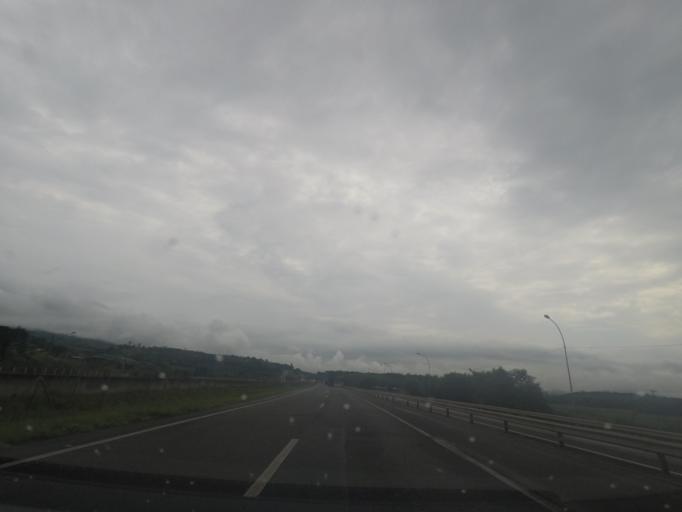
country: BR
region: Sao Paulo
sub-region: Cajati
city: Cajati
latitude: -24.7329
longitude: -48.1131
